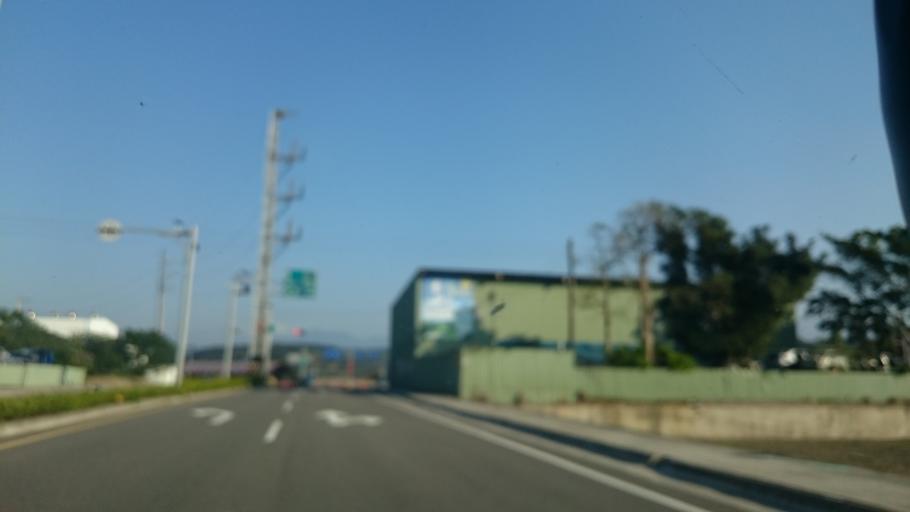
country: TW
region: Taiwan
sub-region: Miaoli
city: Miaoli
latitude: 24.6707
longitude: 120.8837
